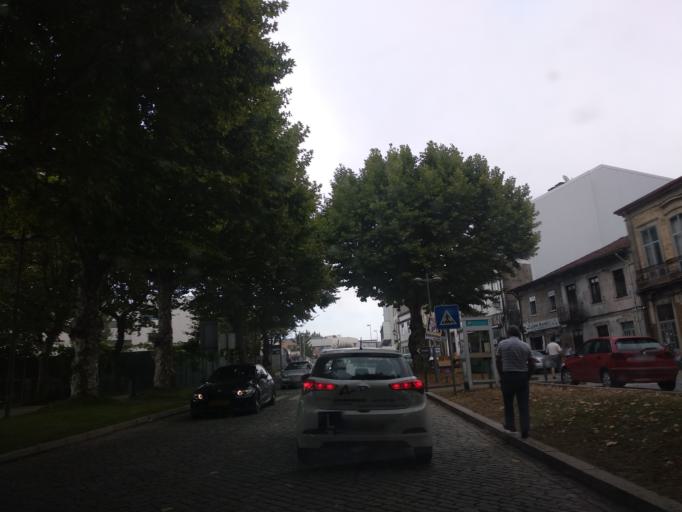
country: PT
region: Braga
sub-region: Vila Verde
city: Vila Verde
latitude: 41.6516
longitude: -8.4347
